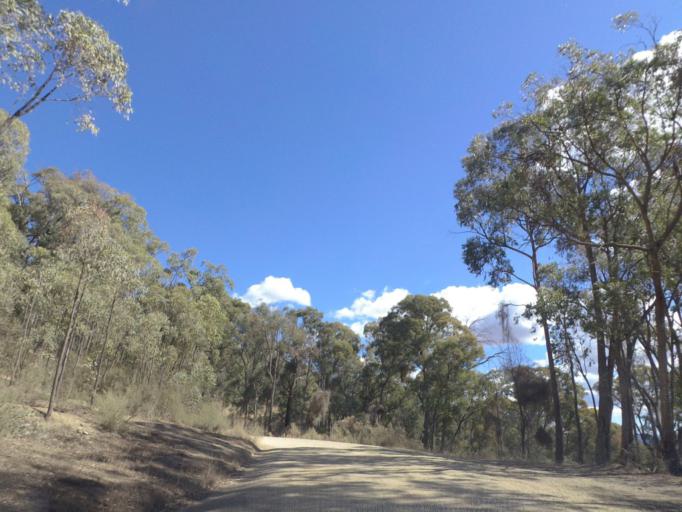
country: AU
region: Victoria
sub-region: Murrindindi
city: Alexandra
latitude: -37.3180
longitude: 145.8115
